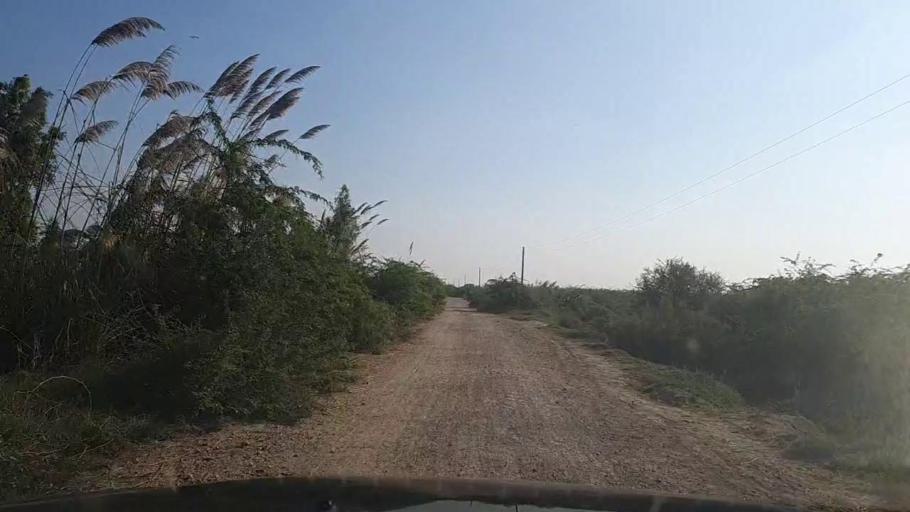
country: PK
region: Sindh
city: Gharo
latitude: 24.7105
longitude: 67.7039
